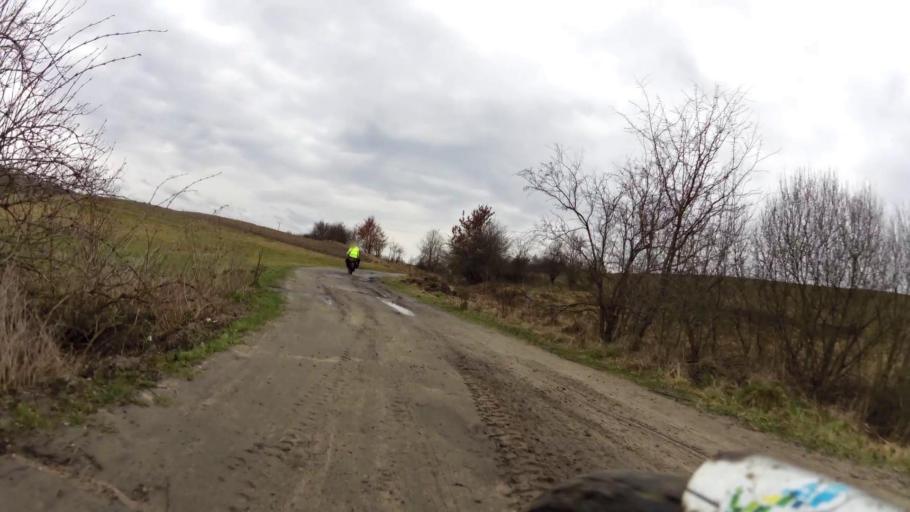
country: PL
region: Pomeranian Voivodeship
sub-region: Powiat bytowski
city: Miastko
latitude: 54.0102
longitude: 16.9926
